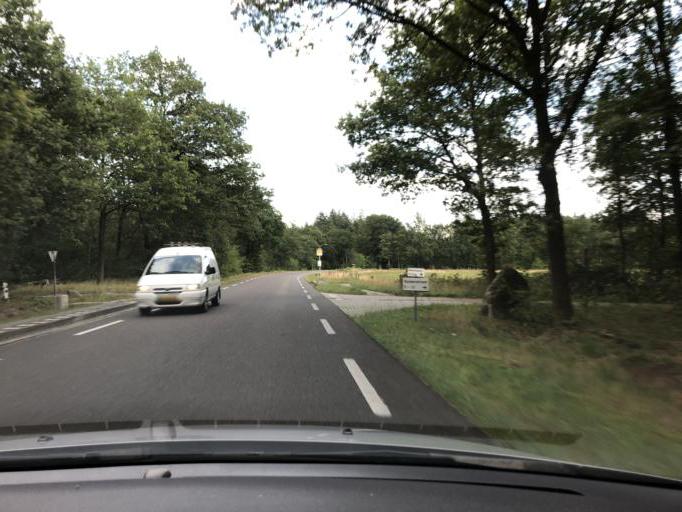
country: NL
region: Drenthe
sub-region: Gemeente Borger-Odoorn
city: Borger
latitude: 52.9383
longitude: 6.7362
